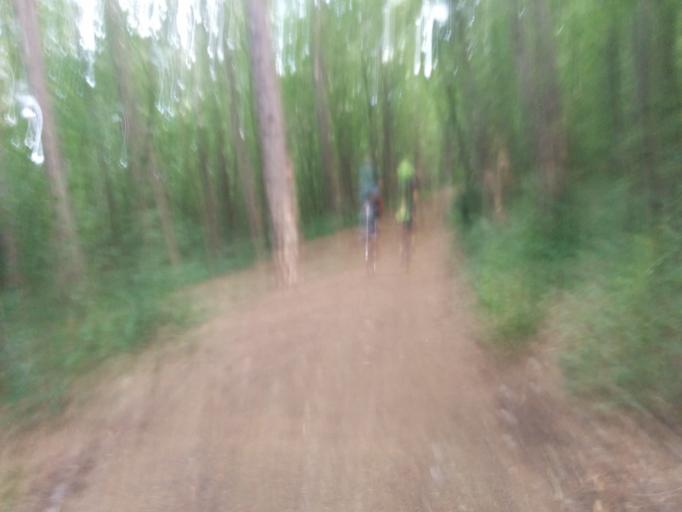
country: AT
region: Lower Austria
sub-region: Politischer Bezirk Modling
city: Gumpoldskirchen
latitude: 48.0540
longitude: 16.2664
